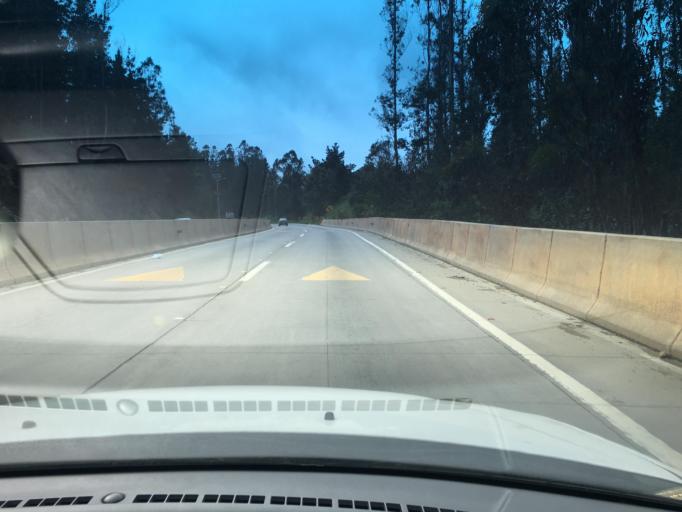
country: CL
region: Valparaiso
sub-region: Provincia de Valparaiso
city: Vina del Mar
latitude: -33.1011
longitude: -71.5729
